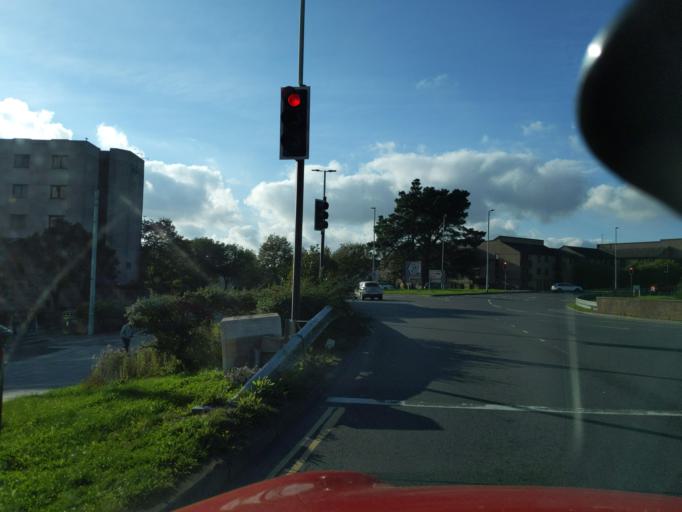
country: GB
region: England
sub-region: Plymouth
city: Plymouth
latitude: 50.3749
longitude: -4.1421
